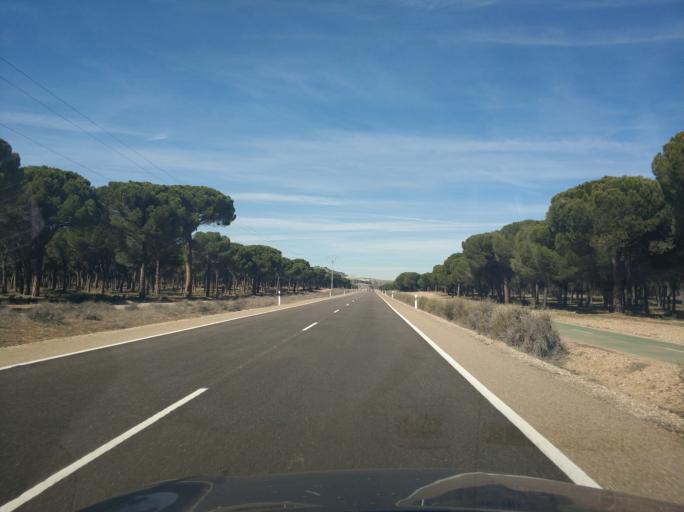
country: ES
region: Castille and Leon
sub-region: Provincia de Valladolid
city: Simancas
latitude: 41.5735
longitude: -4.8079
